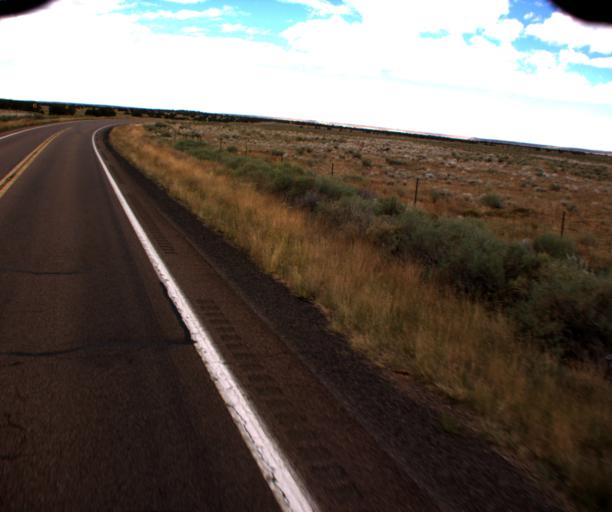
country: US
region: Arizona
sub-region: Navajo County
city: Heber-Overgaard
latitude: 34.5584
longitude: -110.4135
